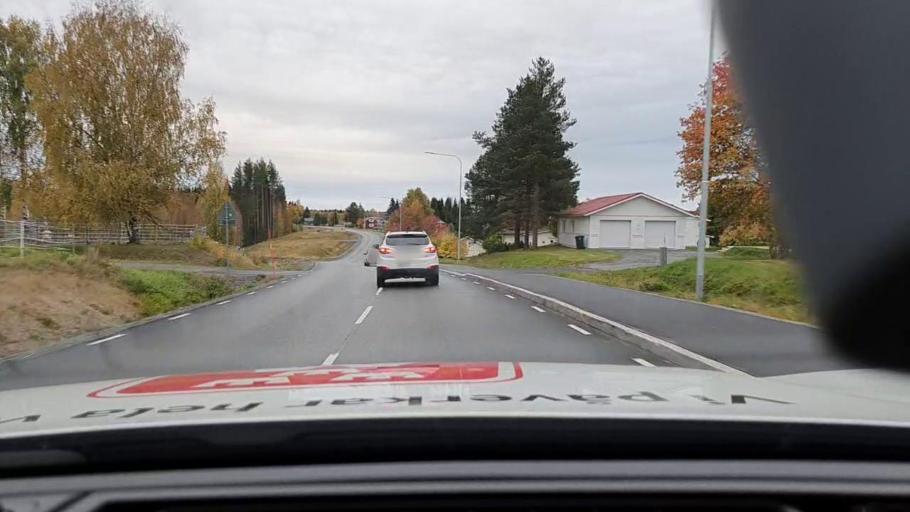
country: SE
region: Norrbotten
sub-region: Bodens Kommun
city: Saevast
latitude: 65.7771
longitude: 21.6931
